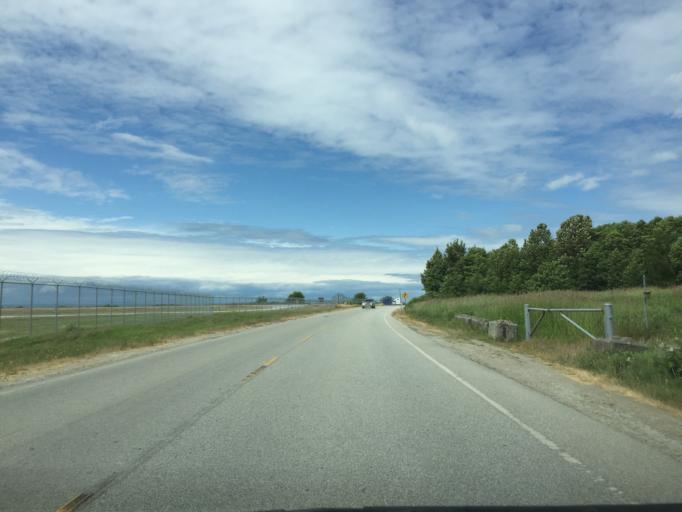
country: CA
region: British Columbia
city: Richmond
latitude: 49.2071
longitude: -123.1990
